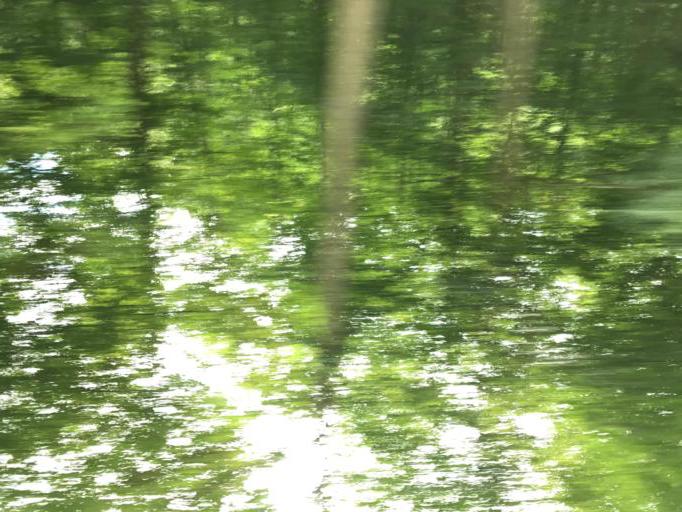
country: DE
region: Baden-Wuerttemberg
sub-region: Tuebingen Region
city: Berg
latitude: 47.8571
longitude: 9.5910
